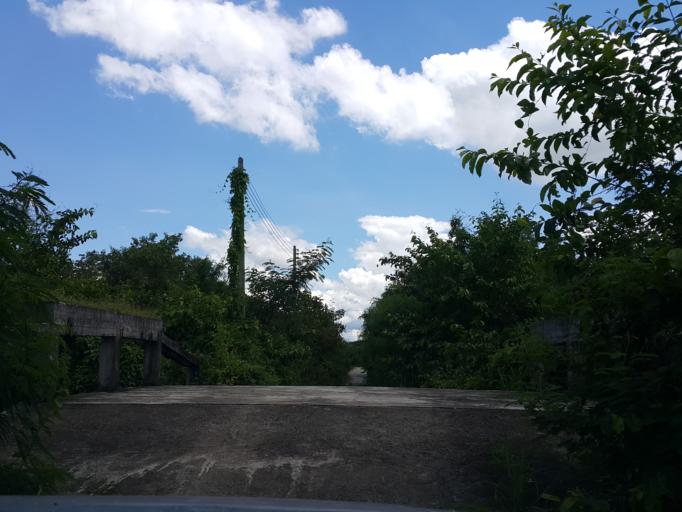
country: TH
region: Chiang Mai
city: San Kamphaeng
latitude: 18.7655
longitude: 99.1198
